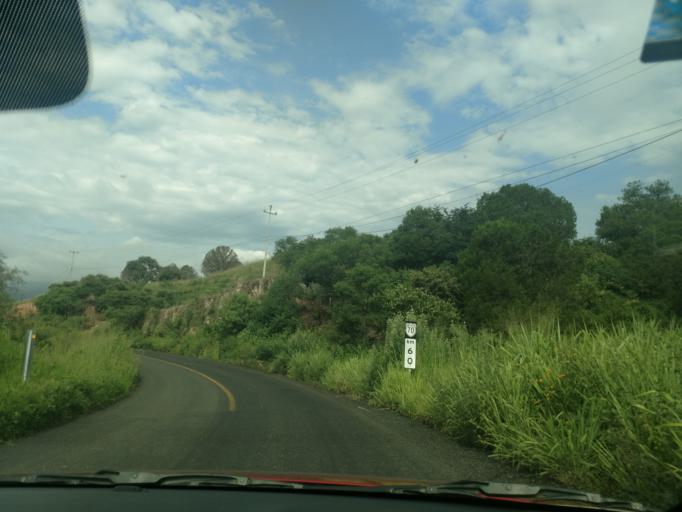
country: MX
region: Jalisco
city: El Salto
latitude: 20.4329
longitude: -104.4778
